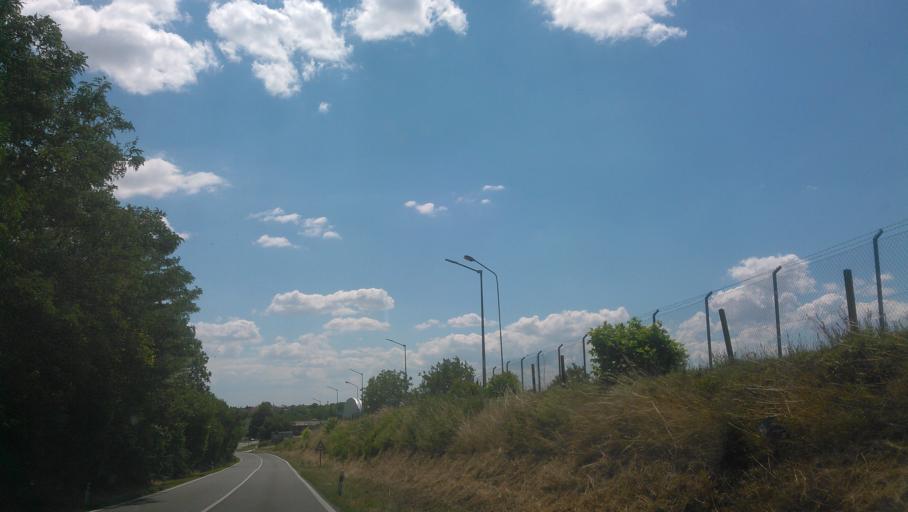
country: SK
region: Trnavsky
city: Leopoldov
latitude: 48.5148
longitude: 17.7256
